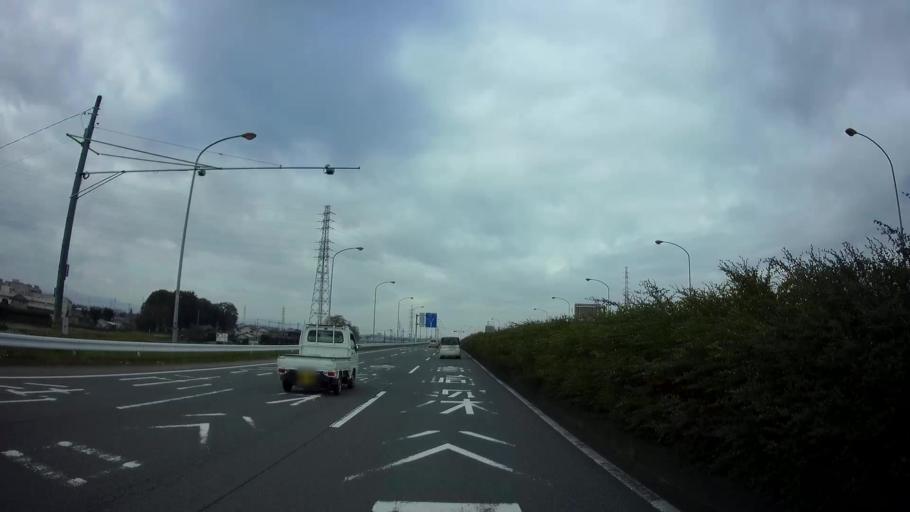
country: JP
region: Saitama
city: Kumagaya
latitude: 36.1733
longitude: 139.3674
